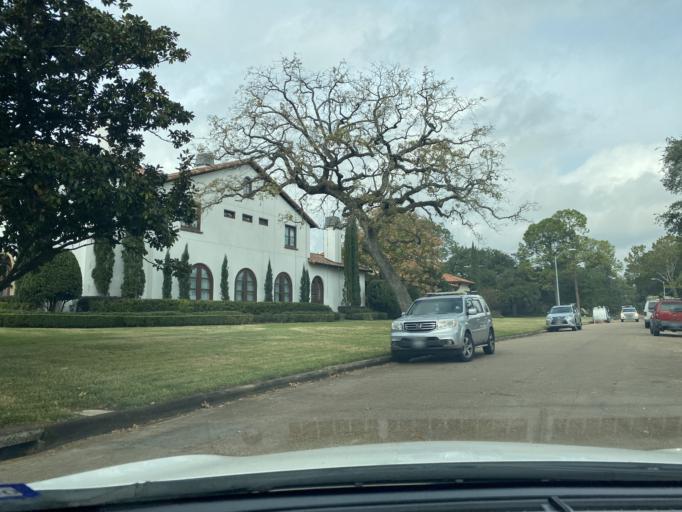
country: US
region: Texas
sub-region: Harris County
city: Hunters Creek Village
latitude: 29.7664
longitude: -95.4753
